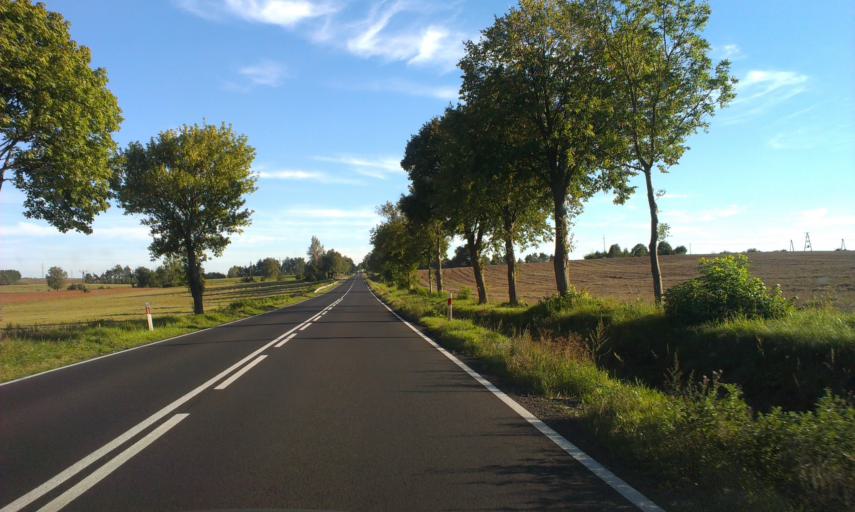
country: PL
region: West Pomeranian Voivodeship
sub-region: Powiat szczecinecki
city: Szczecinek
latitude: 53.7807
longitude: 16.6414
